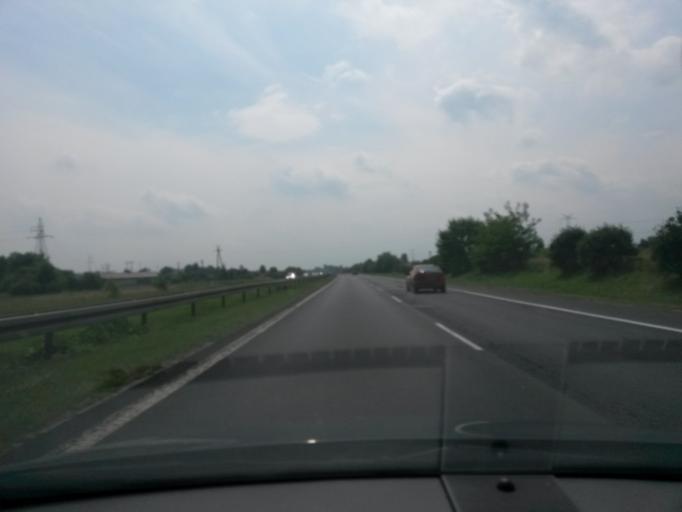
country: PL
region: Lodz Voivodeship
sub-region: Powiat radomszczanski
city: Kamiensk
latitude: 51.2047
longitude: 19.4802
